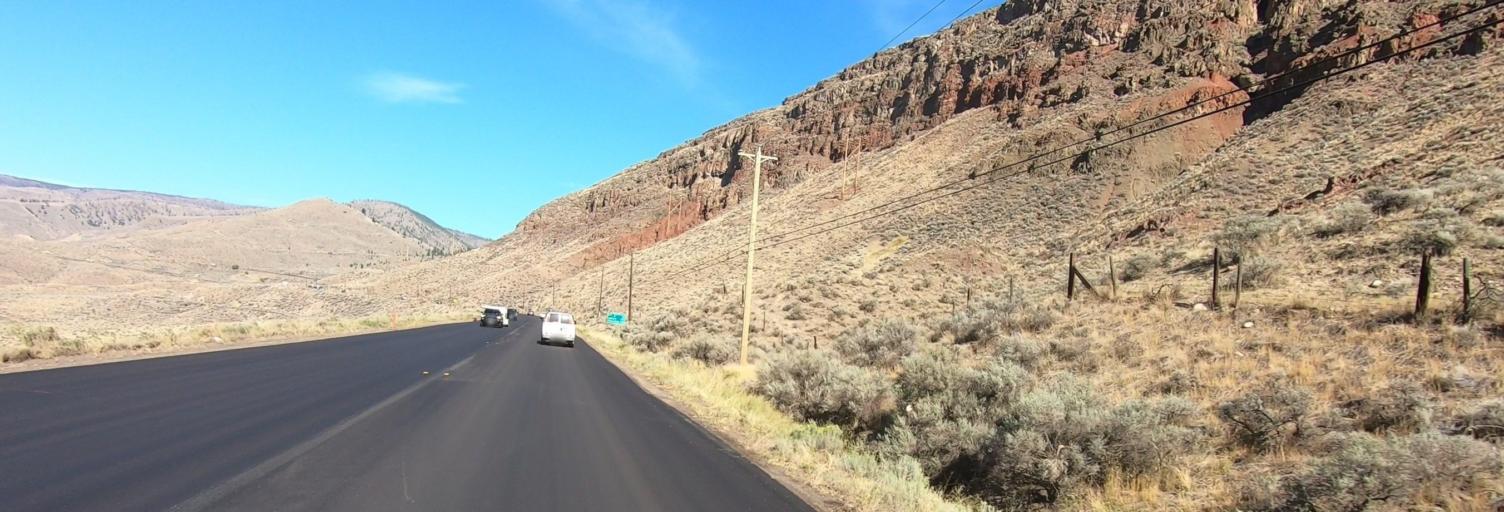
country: CA
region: British Columbia
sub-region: Thompson-Nicola Regional District
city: Ashcroft
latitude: 50.7930
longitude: -121.0885
